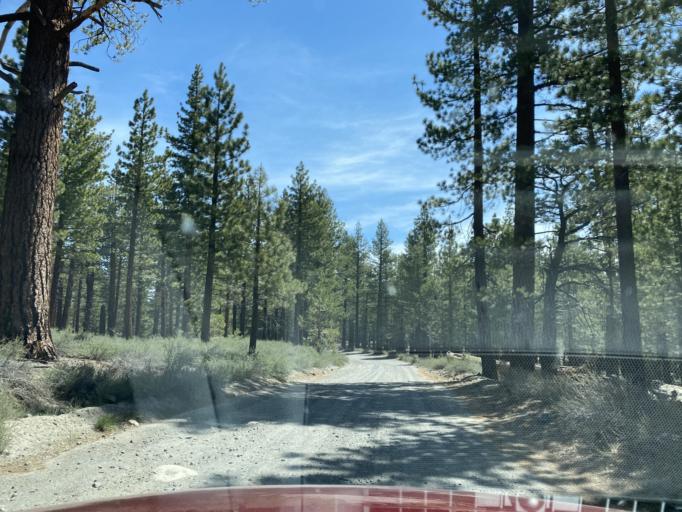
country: US
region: California
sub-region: Mono County
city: Mammoth Lakes
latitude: 37.7694
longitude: -119.0206
